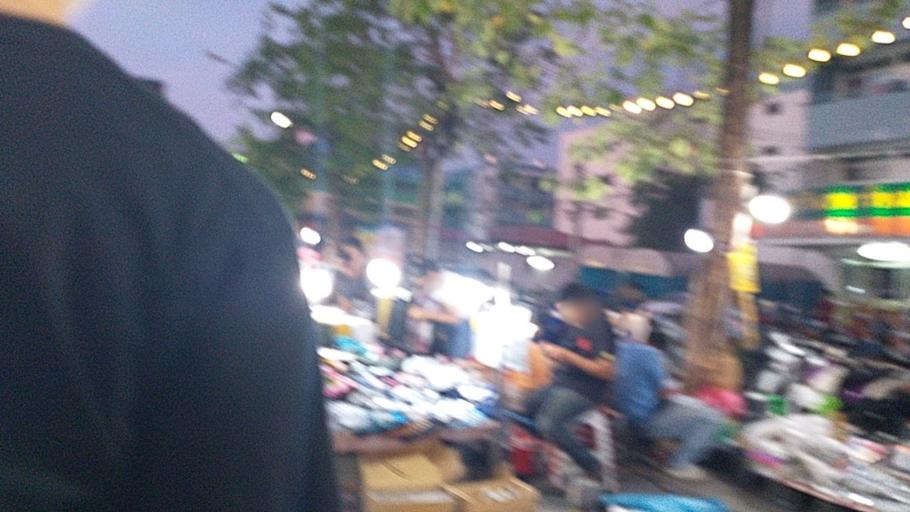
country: TH
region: Bangkok
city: Bang Na
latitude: 13.6690
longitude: 100.6821
